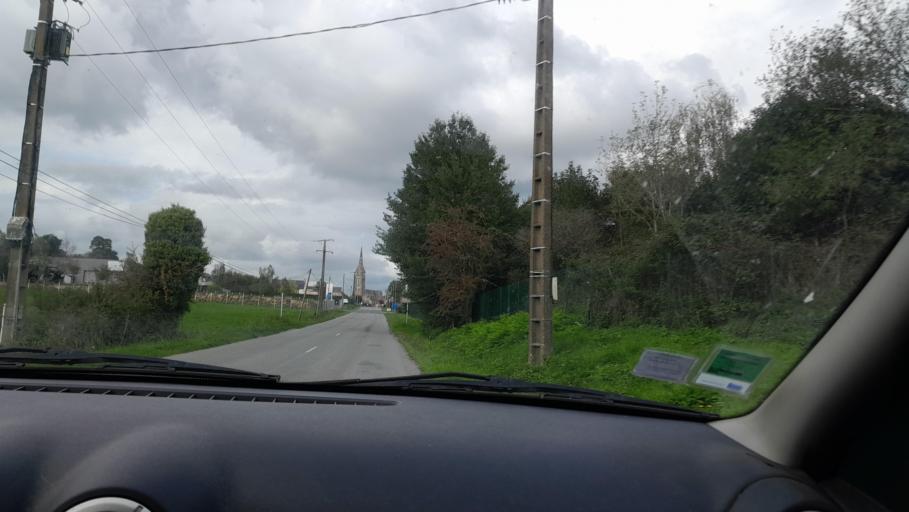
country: FR
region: Brittany
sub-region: Departement d'Ille-et-Vilaine
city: Le Pertre
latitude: 48.0271
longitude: -1.0368
